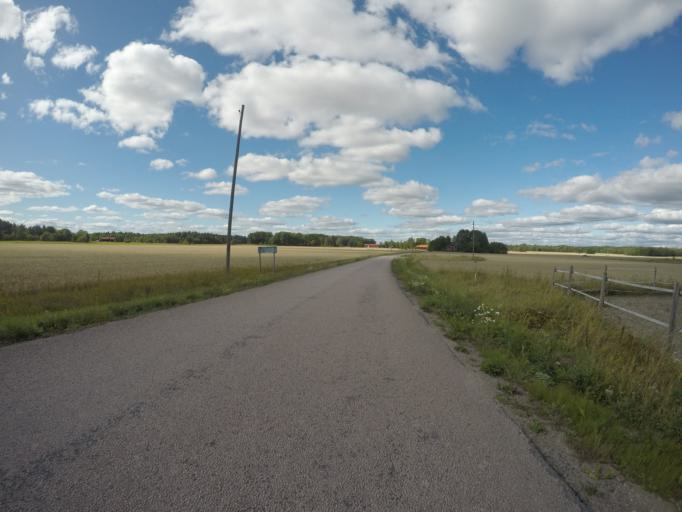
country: SE
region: Vaestmanland
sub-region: Hallstahammars Kommun
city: Kolback
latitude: 59.5081
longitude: 16.1910
